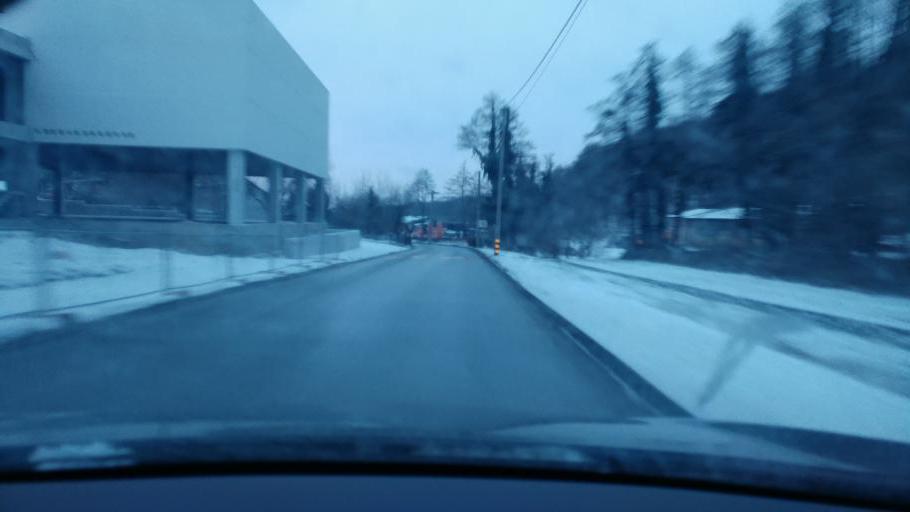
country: HR
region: Grad Zagreb
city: Zagreb
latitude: 45.8586
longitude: 15.9982
